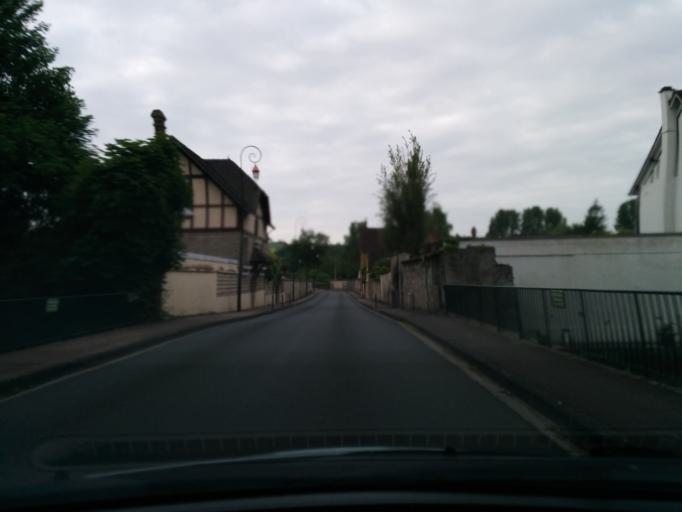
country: FR
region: Haute-Normandie
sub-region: Departement de l'Eure
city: Gasny
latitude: 49.0882
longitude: 1.6080
